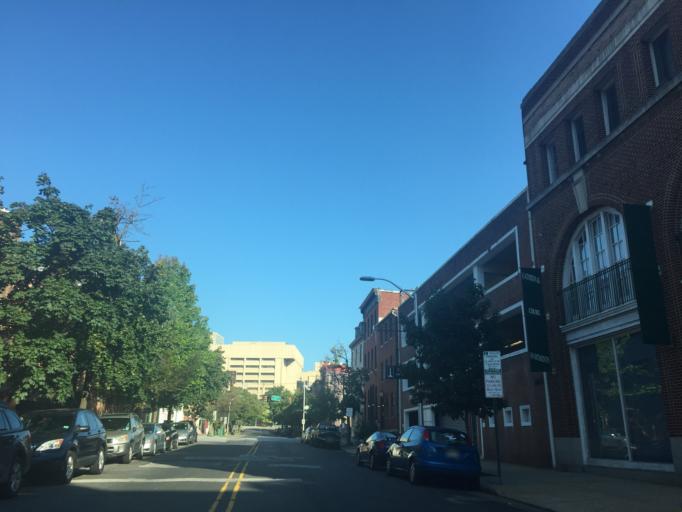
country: US
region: Maryland
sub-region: City of Baltimore
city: Baltimore
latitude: 39.2998
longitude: -76.6179
